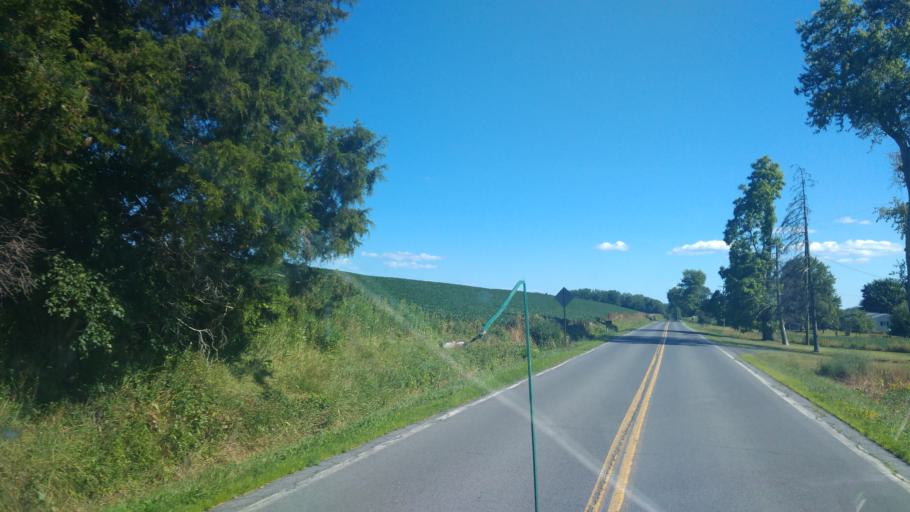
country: US
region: New York
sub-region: Wayne County
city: Clyde
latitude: 43.0193
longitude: -76.8128
